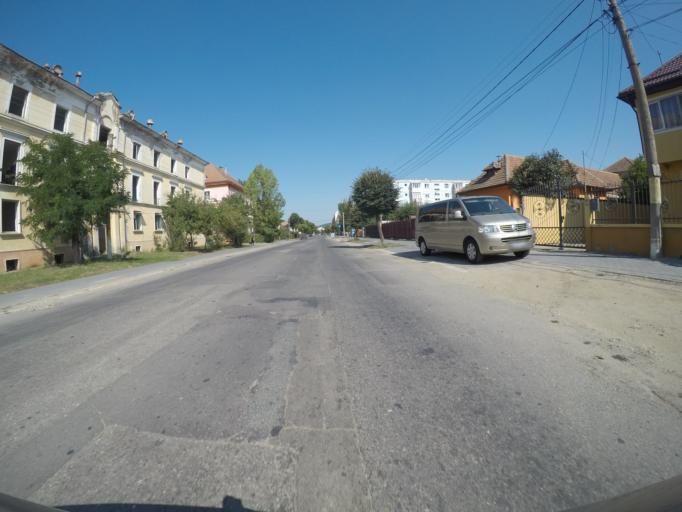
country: RO
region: Brasov
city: Fogarasch
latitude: 45.8336
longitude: 24.9758
